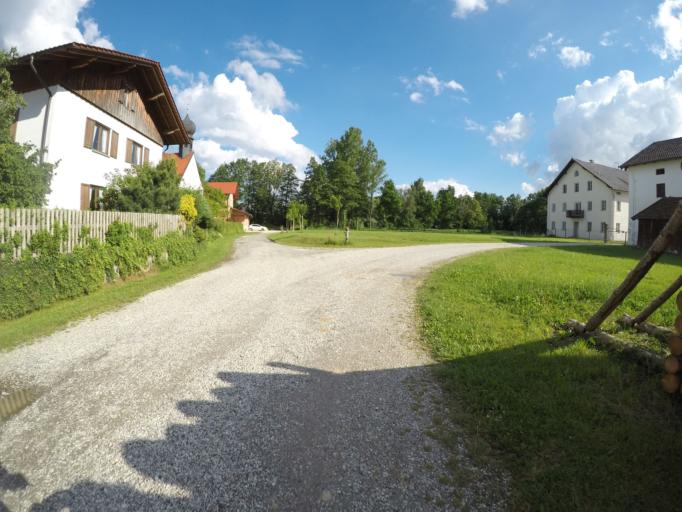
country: DE
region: Bavaria
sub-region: Lower Bavaria
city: Frontenhausen
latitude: 48.5496
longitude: 12.5143
